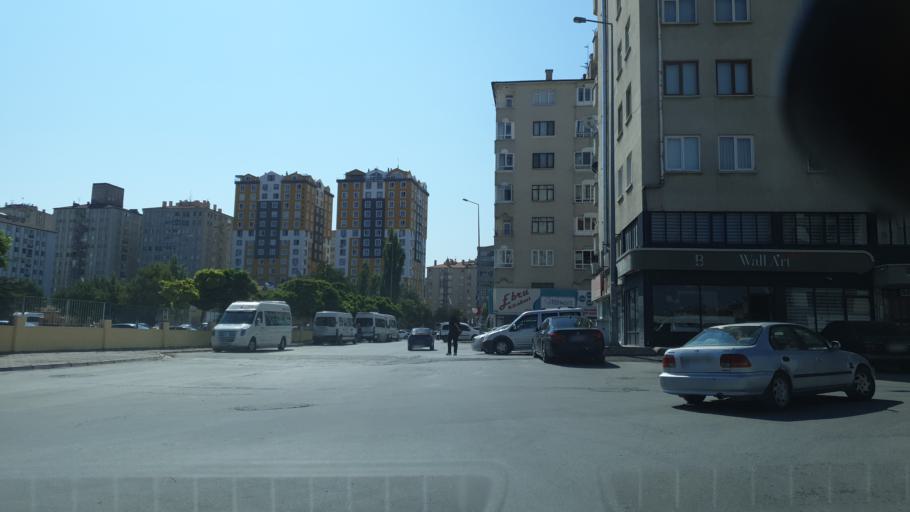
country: TR
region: Kayseri
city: Kayseri
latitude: 38.7264
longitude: 35.4913
